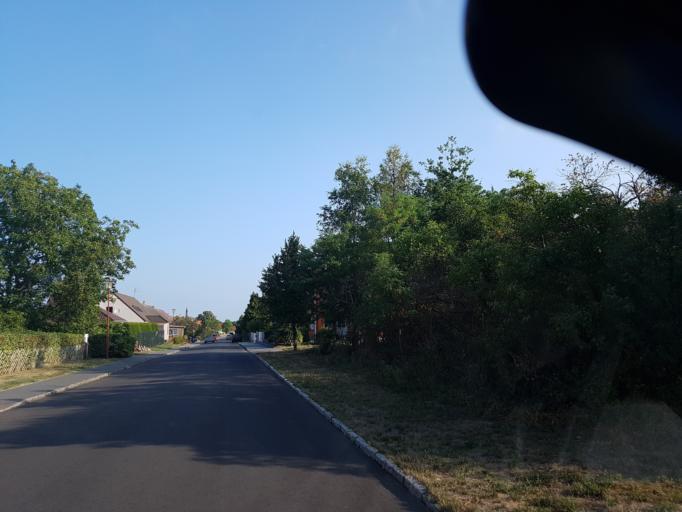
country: DE
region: Brandenburg
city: Niemegk
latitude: 52.0429
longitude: 12.7076
